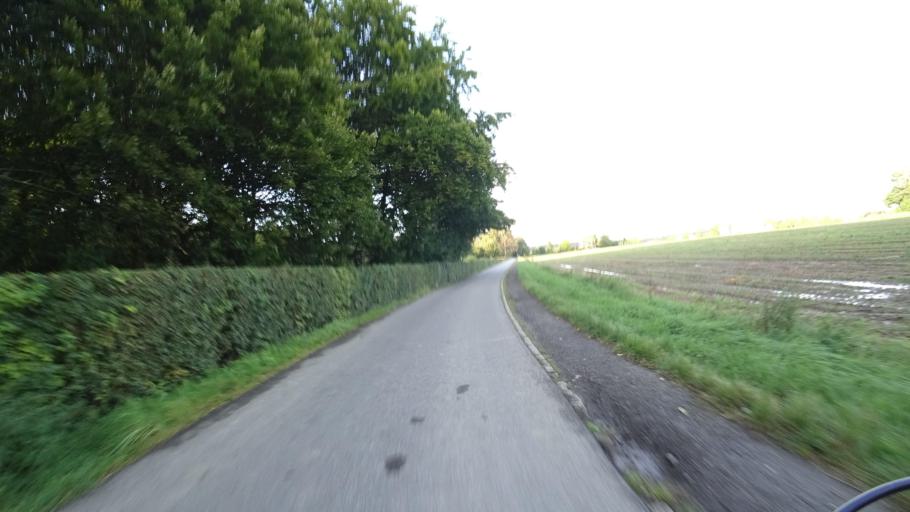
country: BE
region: Wallonia
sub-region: Province de Namur
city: Namur
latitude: 50.4785
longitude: 4.8222
